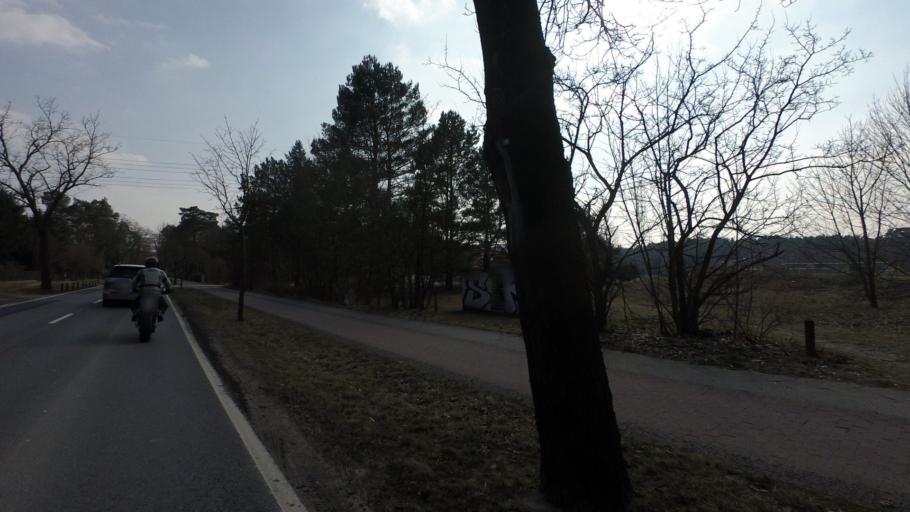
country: DE
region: Brandenburg
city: Potsdam
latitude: 52.3406
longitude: 13.1092
